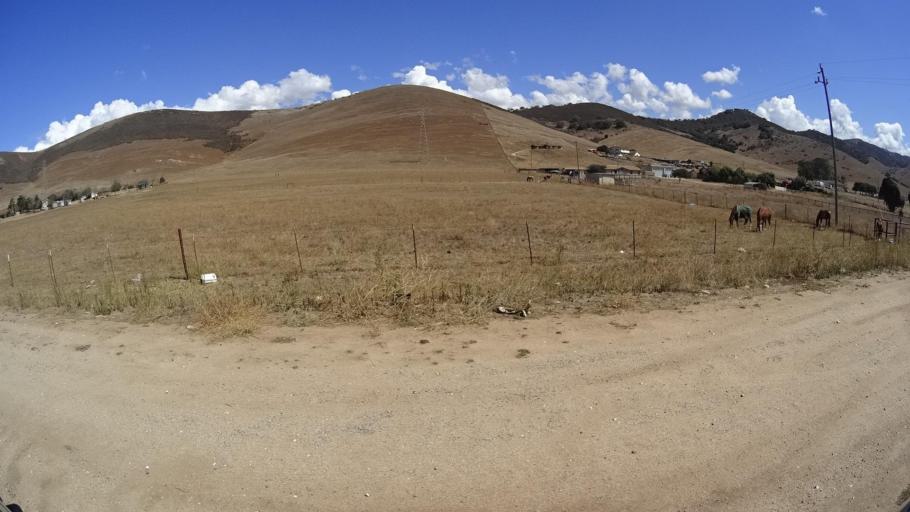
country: US
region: California
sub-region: Monterey County
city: Salinas
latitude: 36.6804
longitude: -121.5569
